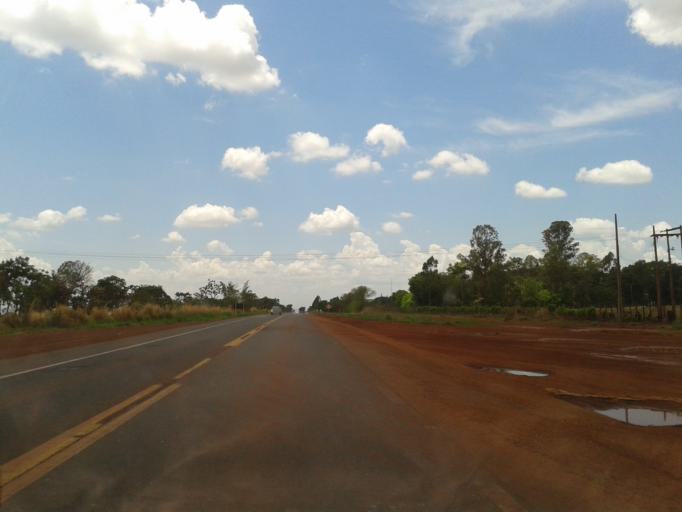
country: BR
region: Goias
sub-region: Goiatuba
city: Goiatuba
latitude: -18.2450
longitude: -49.7001
